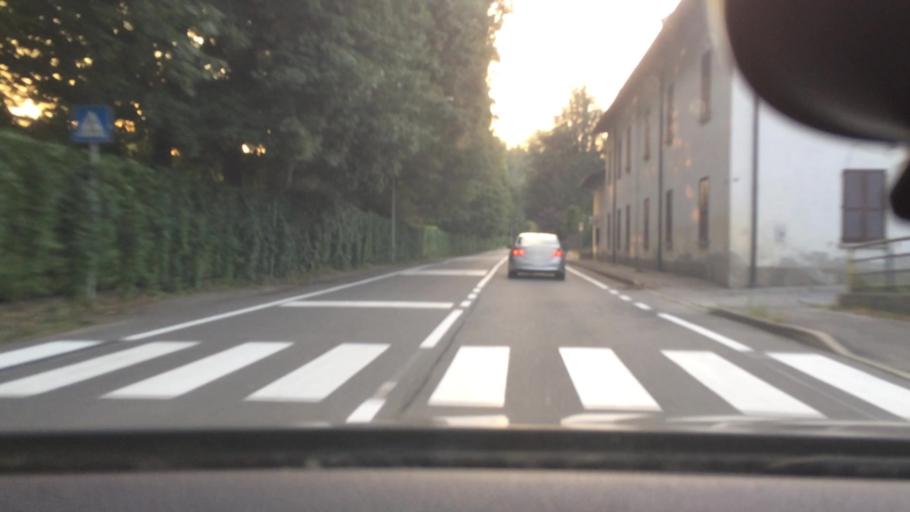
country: IT
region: Lombardy
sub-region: Provincia di Como
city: Anzano del Parco
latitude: 45.7713
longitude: 9.1957
